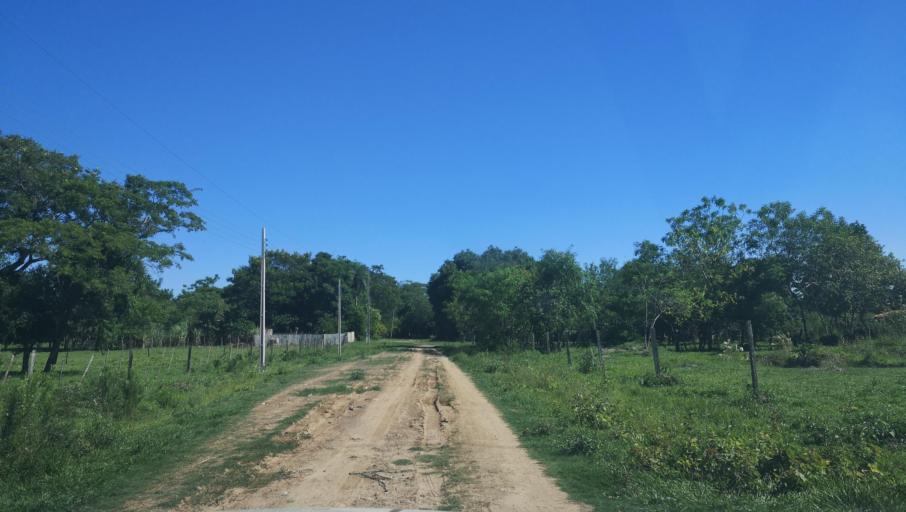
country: PY
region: Caaguazu
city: Carayao
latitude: -25.2008
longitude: -56.3941
